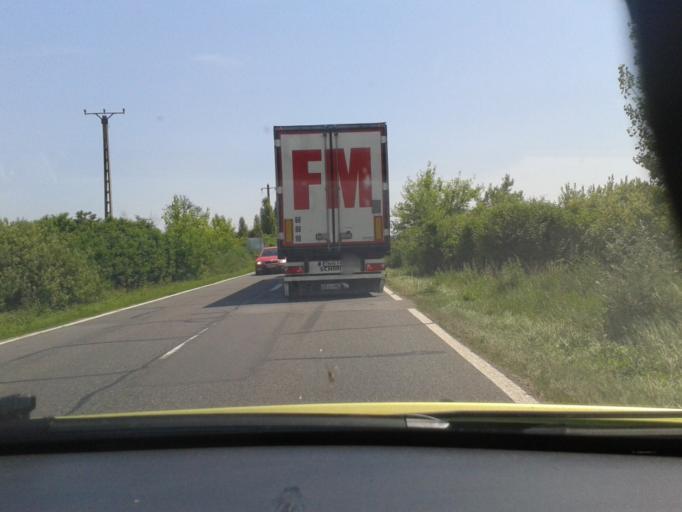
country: RO
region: Timis
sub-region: Comuna Margina
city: Margina
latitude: 45.8583
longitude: 22.2527
